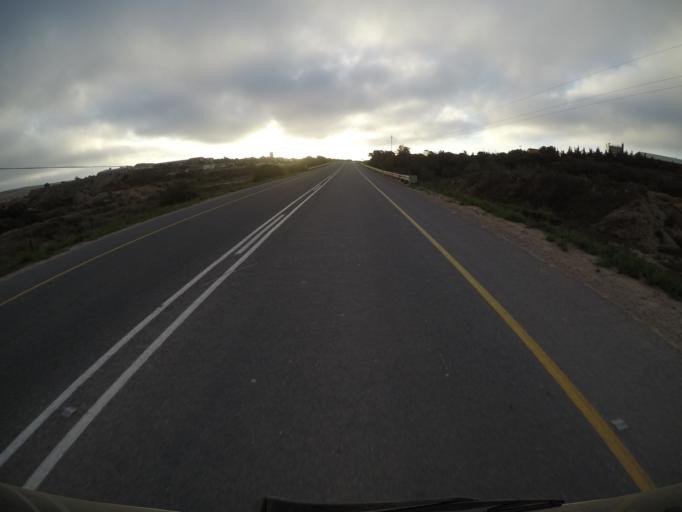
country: ZA
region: Western Cape
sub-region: Eden District Municipality
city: Mossel Bay
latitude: -34.1136
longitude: 22.0819
